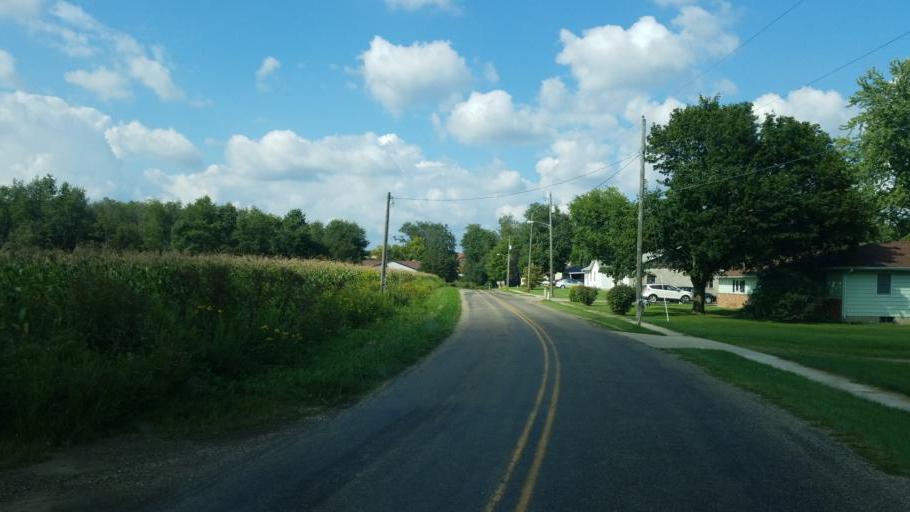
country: US
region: Ohio
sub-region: Knox County
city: Gambier
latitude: 40.4055
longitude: -82.3320
